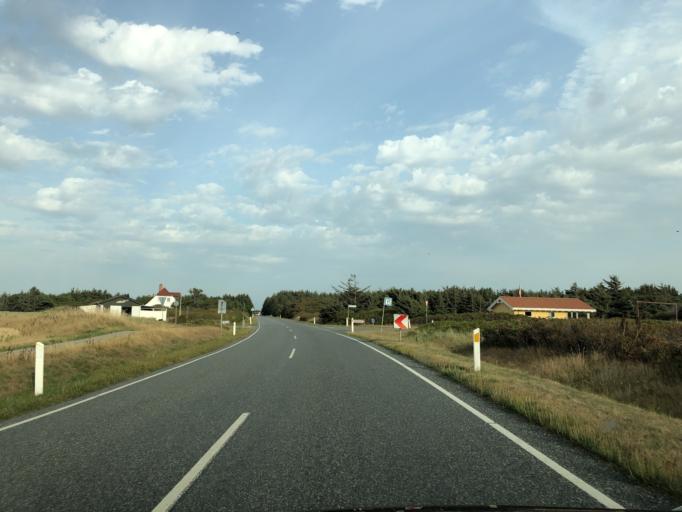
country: DK
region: Central Jutland
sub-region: Holstebro Kommune
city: Ulfborg
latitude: 56.3220
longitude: 8.1266
